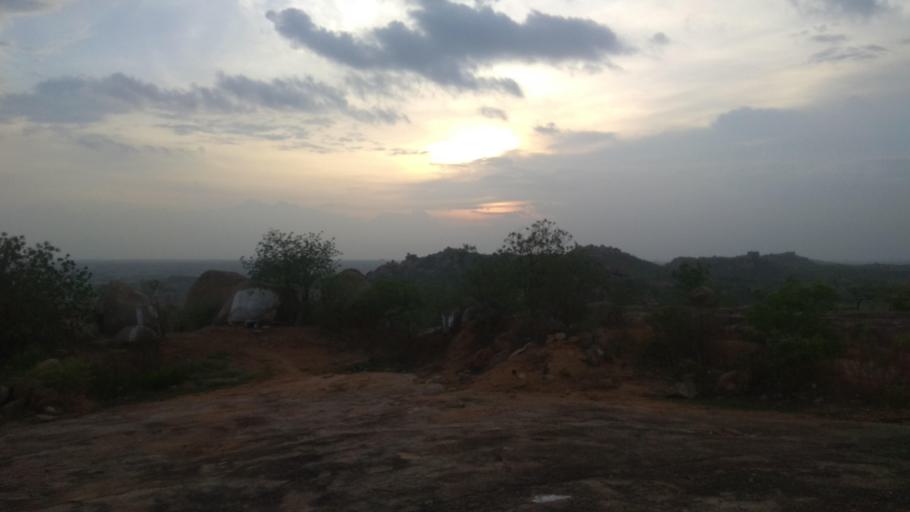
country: IN
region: Telangana
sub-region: Mahbubnagar
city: Farrukhnagar
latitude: 16.8893
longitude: 78.5051
